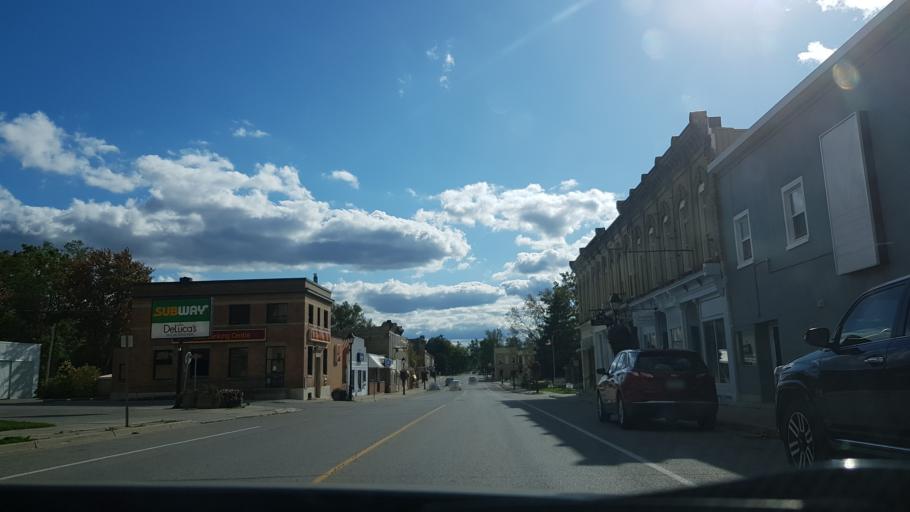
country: CA
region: Ontario
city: South Huron
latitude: 43.1641
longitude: -81.6837
